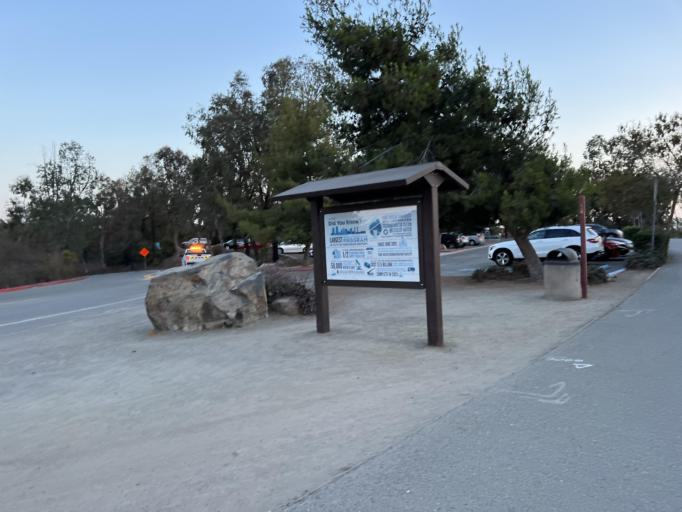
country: US
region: California
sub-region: San Diego County
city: Poway
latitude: 32.9131
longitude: -117.1023
